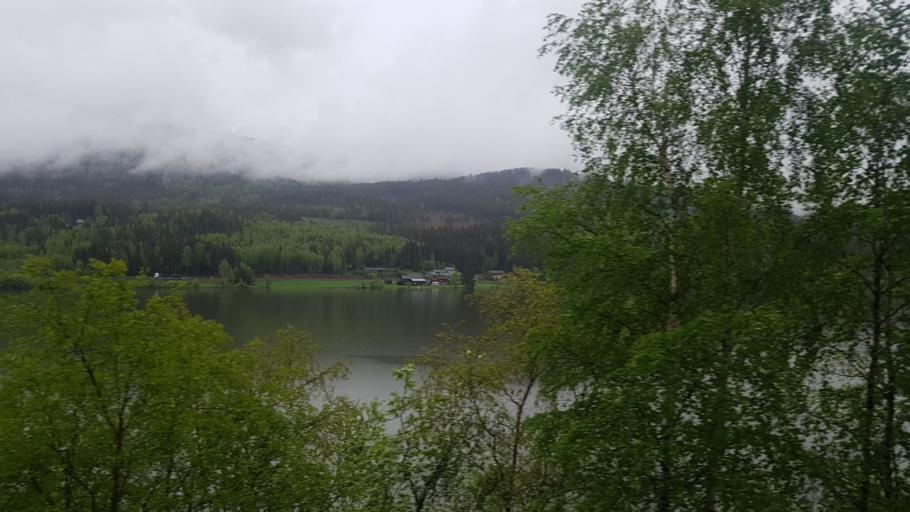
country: NO
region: Oppland
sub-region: Oyer
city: Tretten
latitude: 61.3088
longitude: 10.2918
